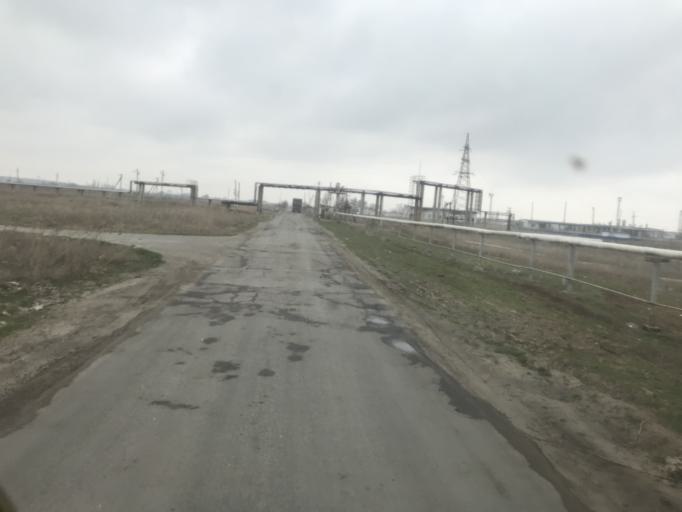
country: RU
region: Volgograd
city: Svetlyy Yar
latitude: 48.5131
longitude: 44.6350
